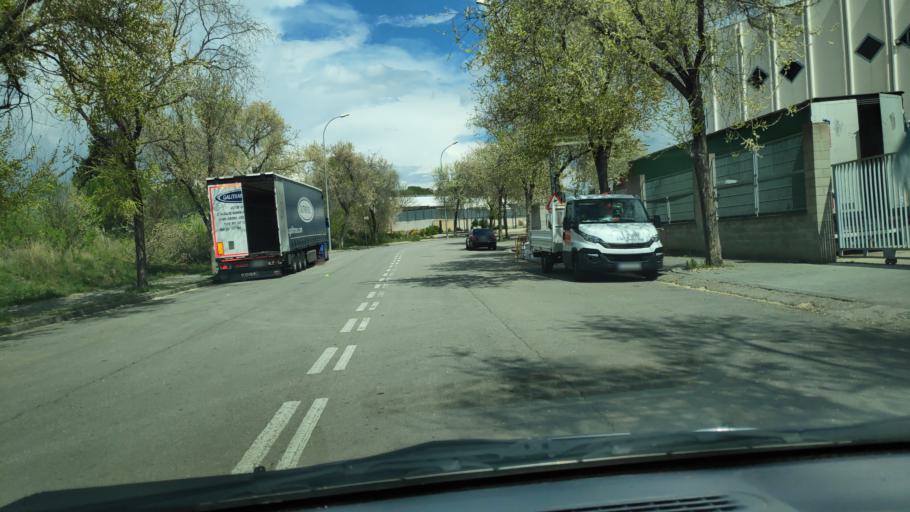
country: ES
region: Catalonia
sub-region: Provincia de Barcelona
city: Sabadell
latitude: 41.5367
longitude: 2.1291
